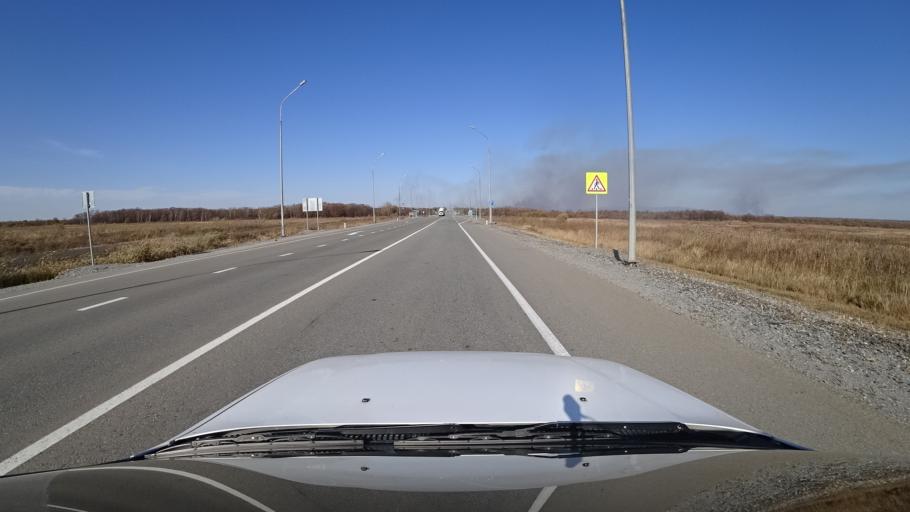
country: RU
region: Primorskiy
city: Dal'nerechensk
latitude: 45.8657
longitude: 133.7211
